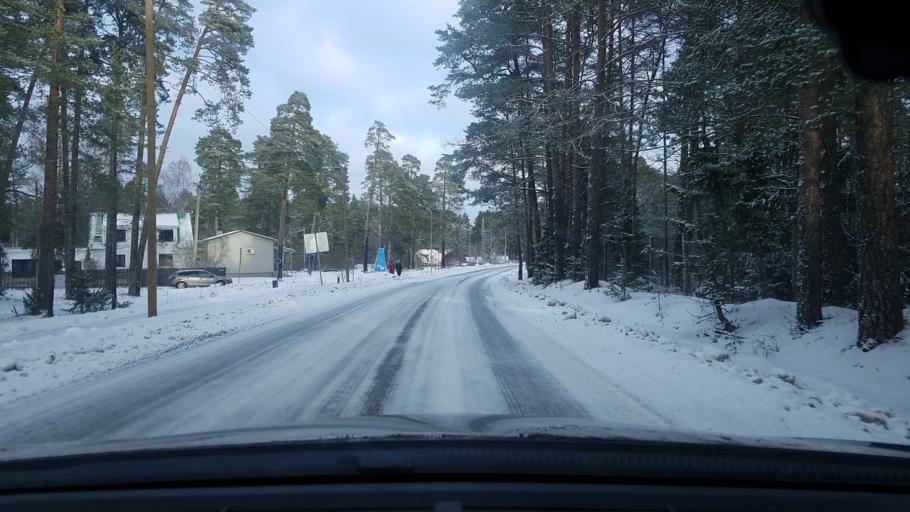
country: EE
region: Harju
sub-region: Keila linn
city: Keila
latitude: 59.3196
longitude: 24.2510
